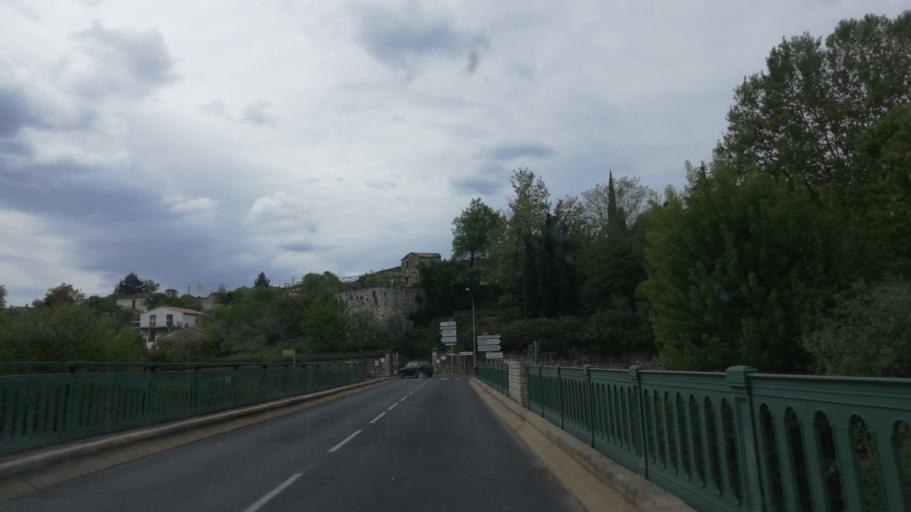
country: FR
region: Languedoc-Roussillon
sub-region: Departement de l'Herault
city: Ganges
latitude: 43.9307
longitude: 3.7029
